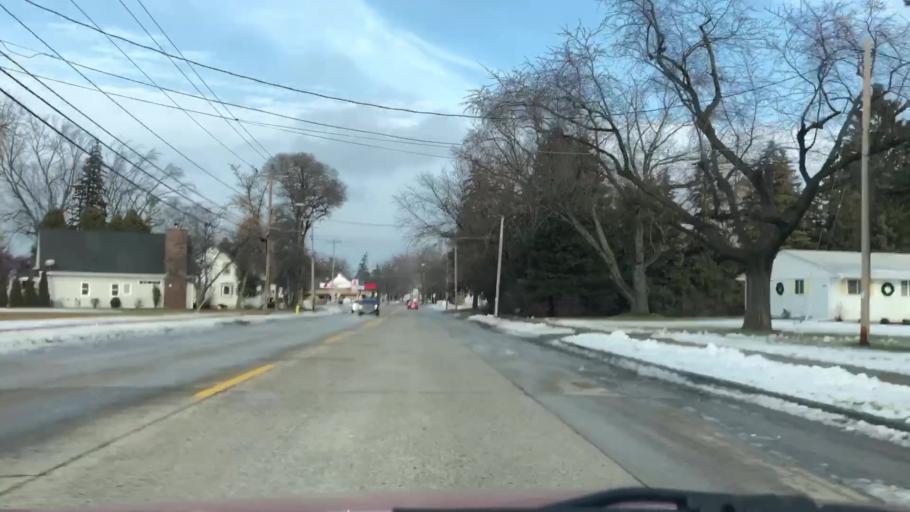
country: US
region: Wisconsin
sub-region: Brown County
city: De Pere
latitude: 44.4362
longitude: -88.0732
